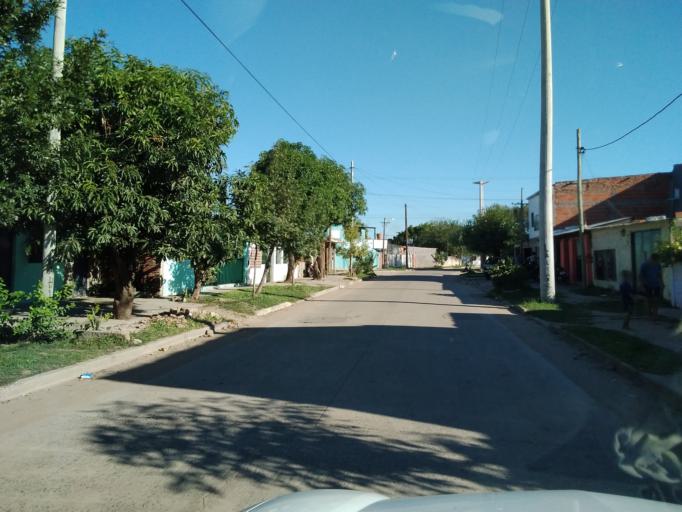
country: AR
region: Corrientes
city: Corrientes
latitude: -27.4733
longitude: -58.7918
